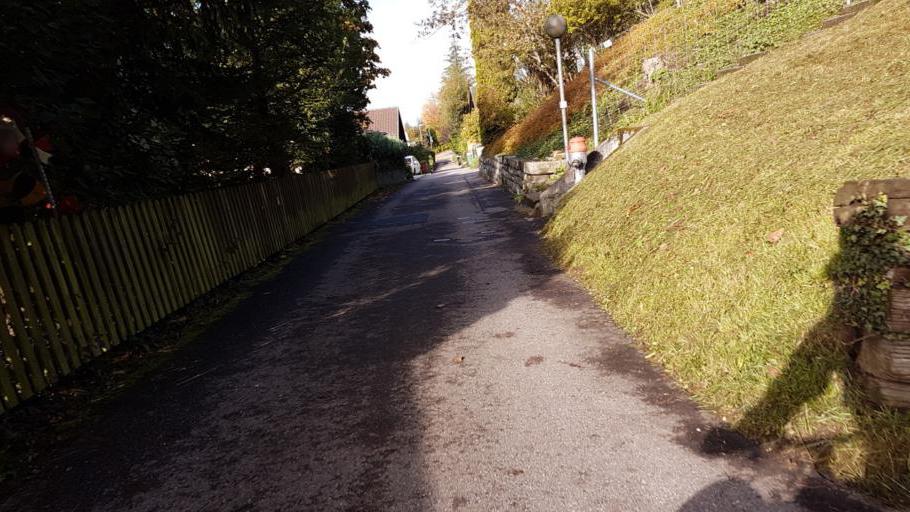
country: CH
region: Bern
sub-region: Bern-Mittelland District
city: Stettlen
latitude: 46.9341
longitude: 7.5283
